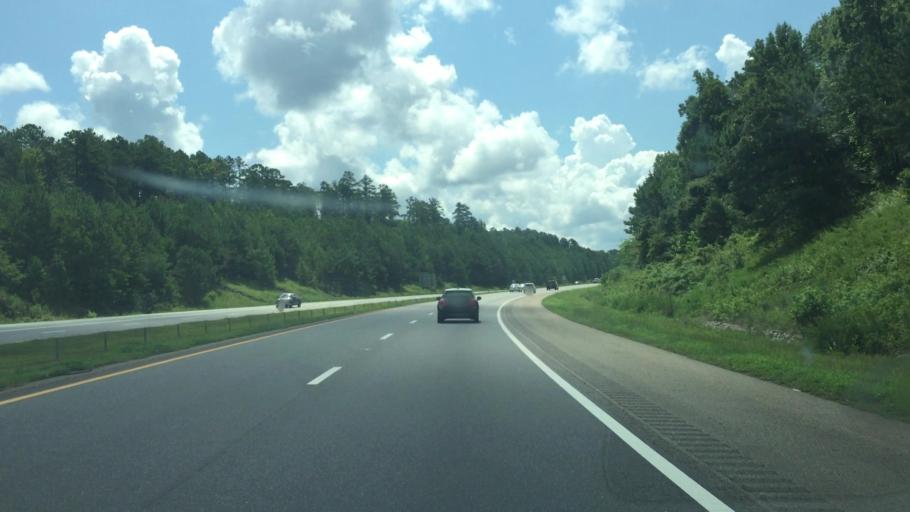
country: US
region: North Carolina
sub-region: Richmond County
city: Cordova
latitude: 34.9453
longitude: -79.8470
